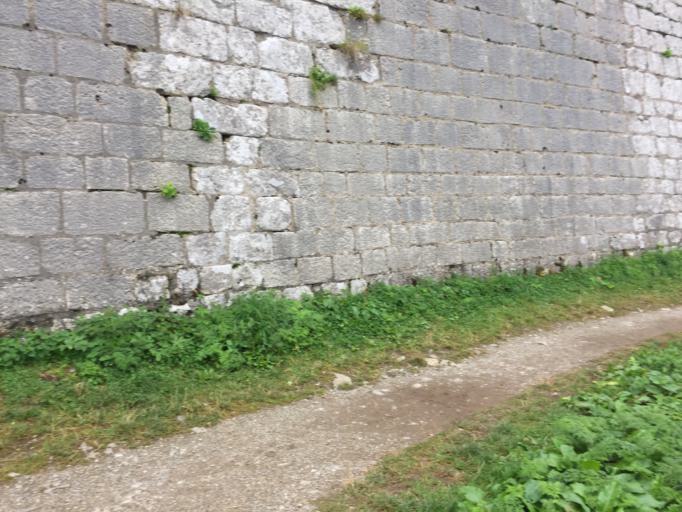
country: FR
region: Midi-Pyrenees
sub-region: Departement de l'Ariege
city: Lavelanet
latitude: 42.8757
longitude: 1.8327
